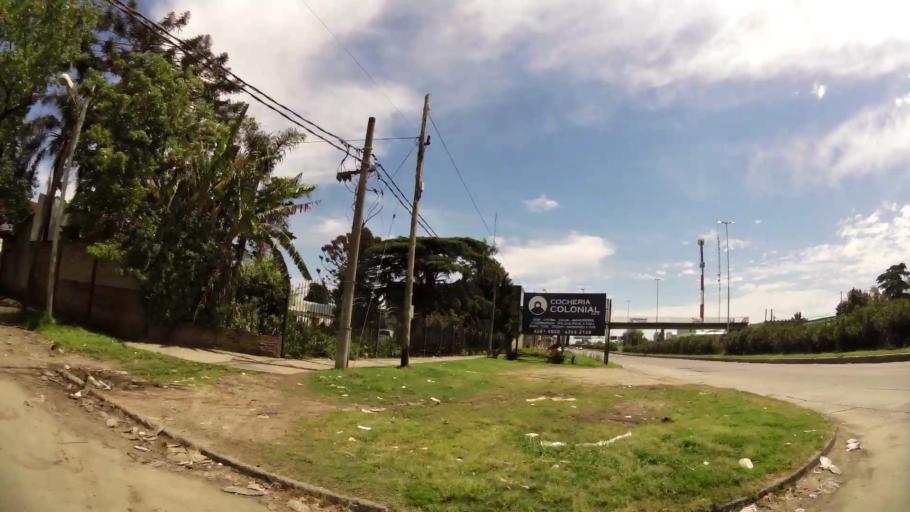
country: AR
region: Buenos Aires
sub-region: Partido de Quilmes
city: Quilmes
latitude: -34.7860
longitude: -58.2572
